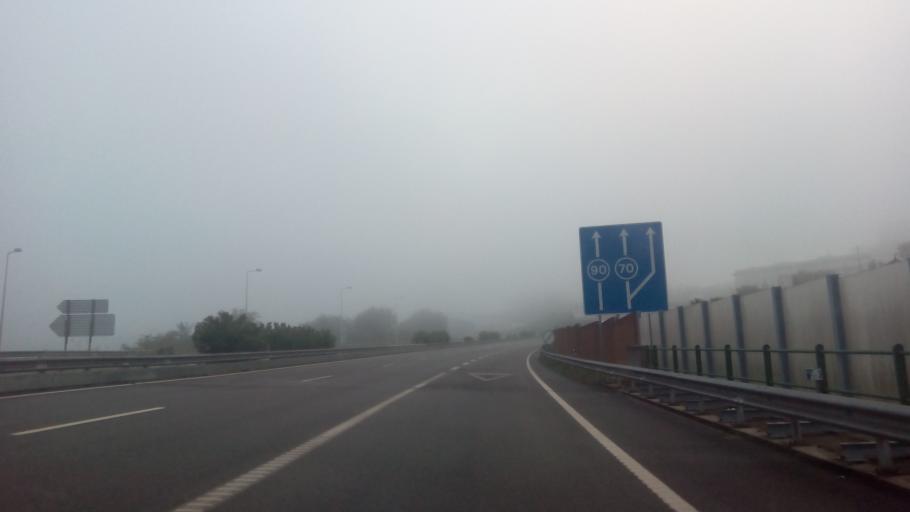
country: PT
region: Porto
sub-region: Penafiel
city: Penafiel
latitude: 41.2120
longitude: -8.2874
